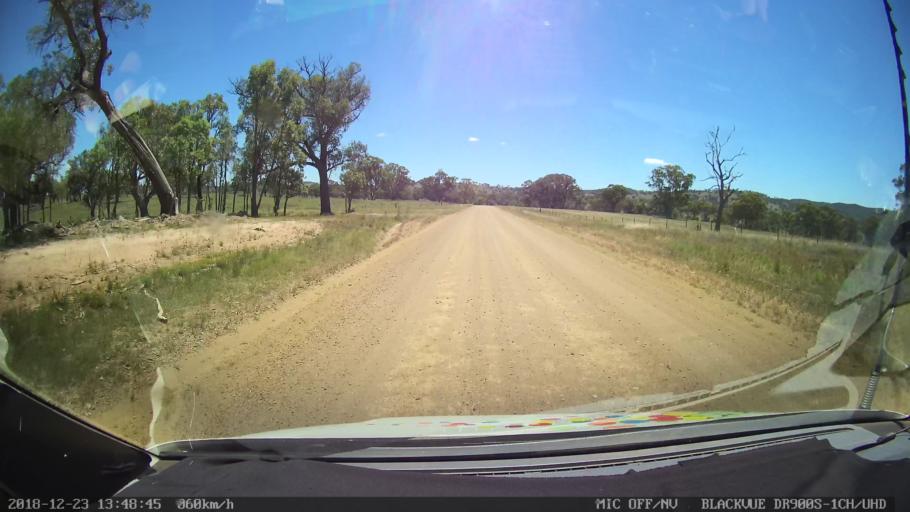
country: AU
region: New South Wales
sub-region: Tamworth Municipality
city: Manilla
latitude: -30.5193
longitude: 151.1143
